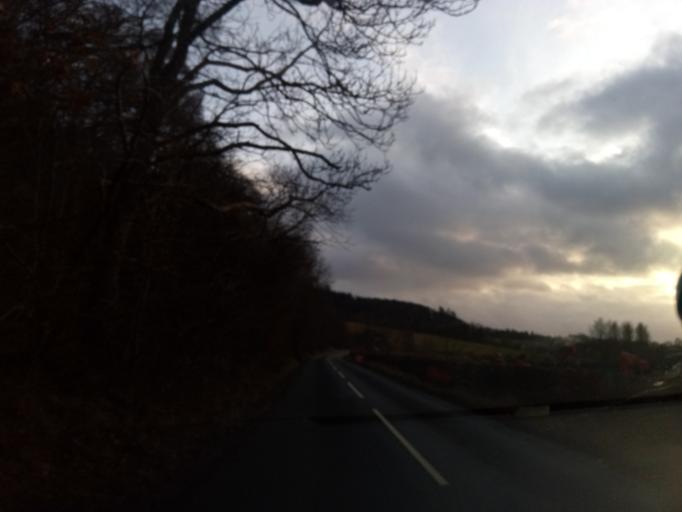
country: GB
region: Scotland
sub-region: The Scottish Borders
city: Galashiels
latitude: 55.5822
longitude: -2.8083
